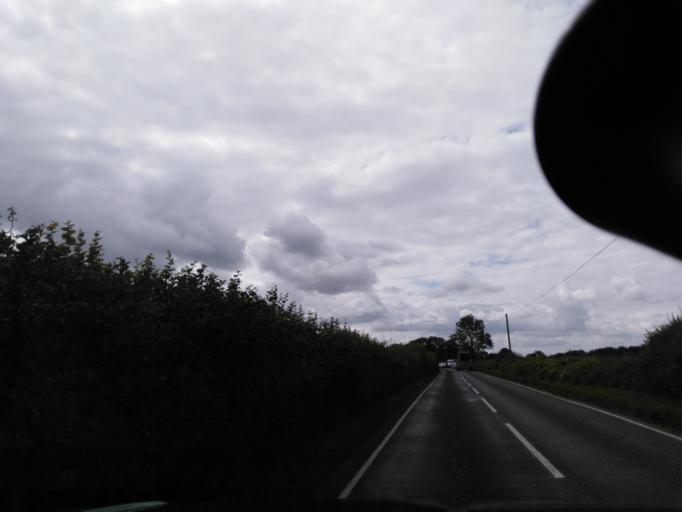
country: GB
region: England
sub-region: Dorset
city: Blandford Forum
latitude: 50.8921
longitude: -2.1576
